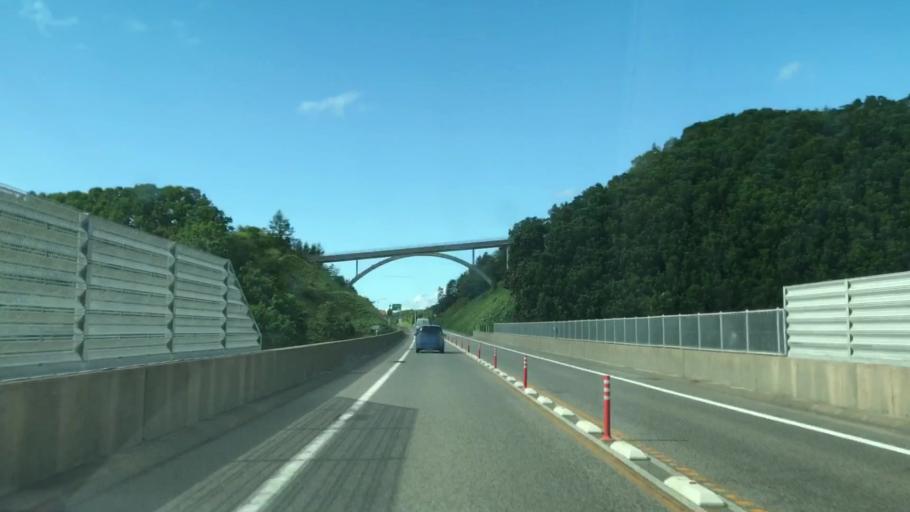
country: JP
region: Hokkaido
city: Date
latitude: 42.4597
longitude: 140.9116
